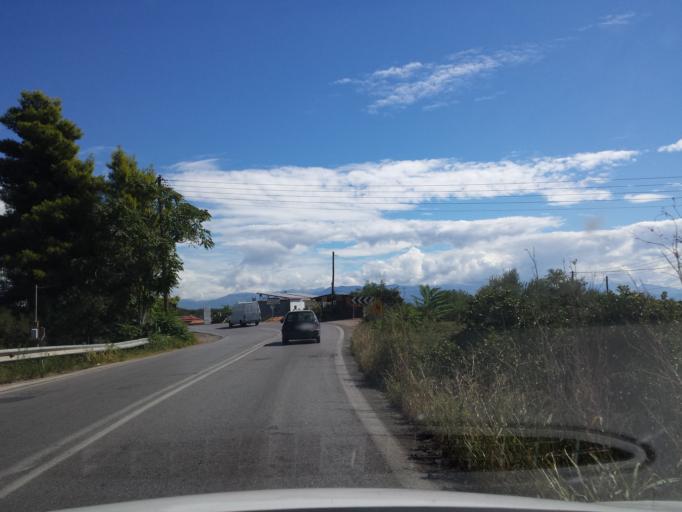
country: GR
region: Peloponnese
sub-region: Nomos Messinias
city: Messini
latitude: 37.0048
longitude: 21.9296
